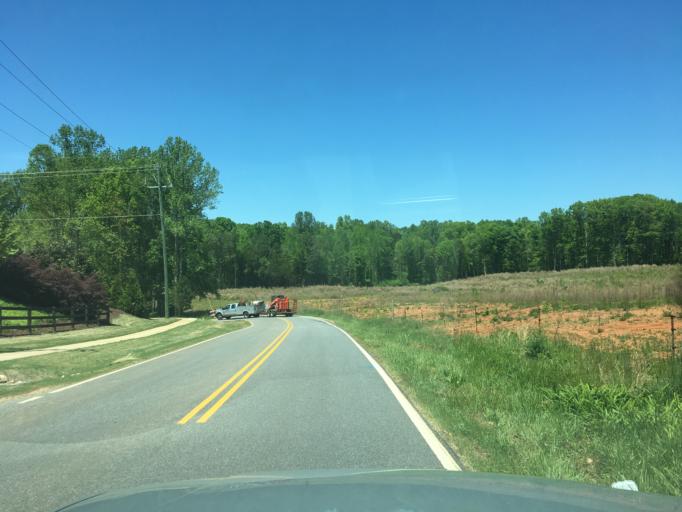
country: US
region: South Carolina
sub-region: Spartanburg County
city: Duncan
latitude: 34.8621
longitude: -82.1499
